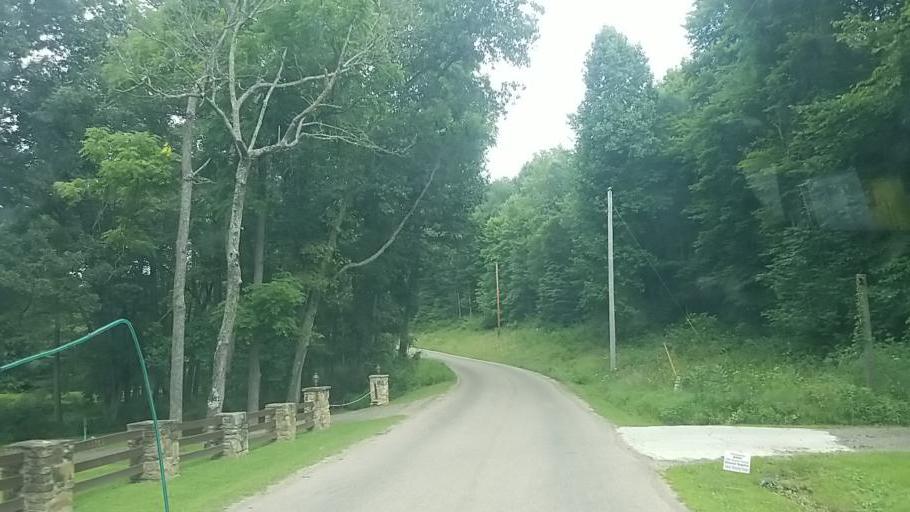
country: US
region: Ohio
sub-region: Licking County
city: Utica
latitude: 40.2458
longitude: -82.2907
